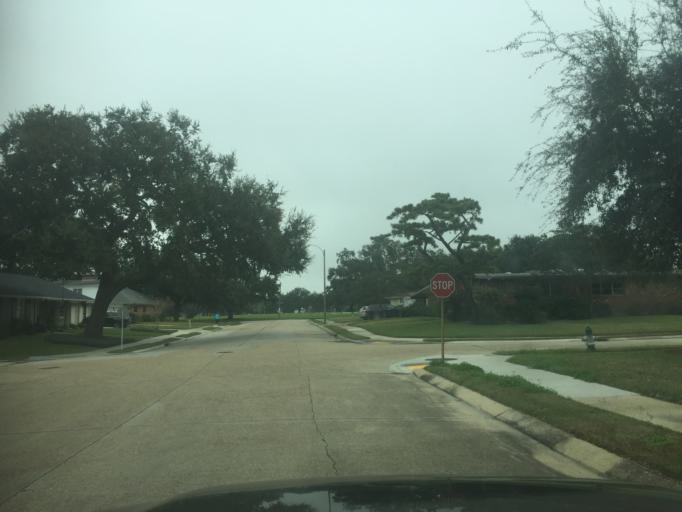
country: US
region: Louisiana
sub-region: Jefferson Parish
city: Metairie
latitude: 30.0206
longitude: -90.1047
